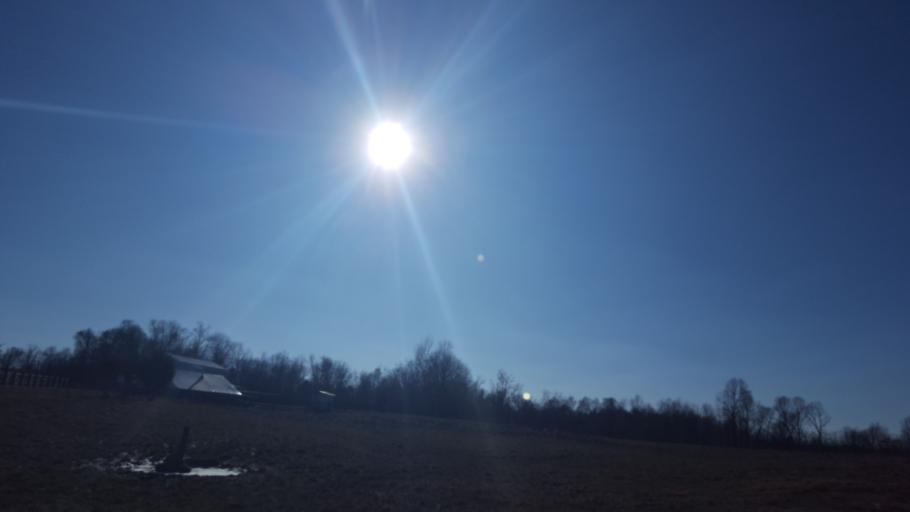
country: US
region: Kentucky
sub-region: Crittenden County
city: Marion
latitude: 37.4372
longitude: -88.0509
